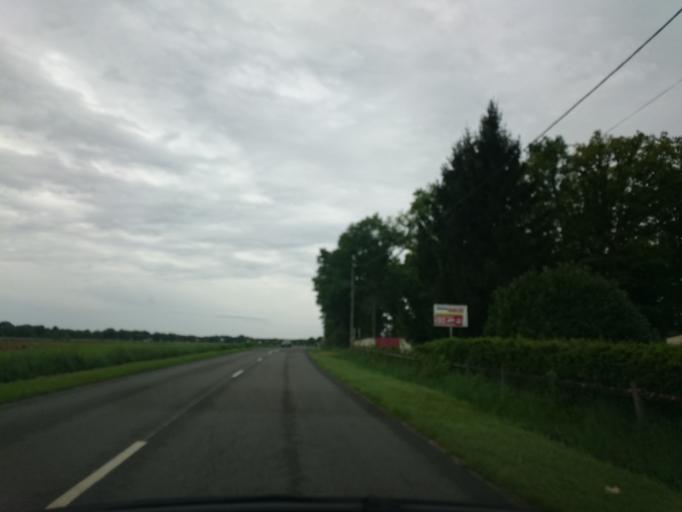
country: FR
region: Centre
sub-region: Departement du Loir-et-Cher
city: Muides-sur-Loire
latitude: 47.6650
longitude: 1.5338
